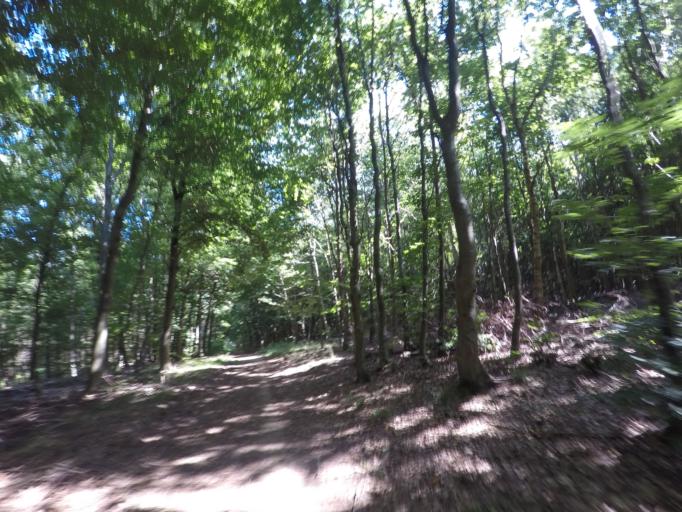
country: LU
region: Luxembourg
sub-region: Canton de Capellen
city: Kopstal
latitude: 49.6496
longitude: 6.0688
